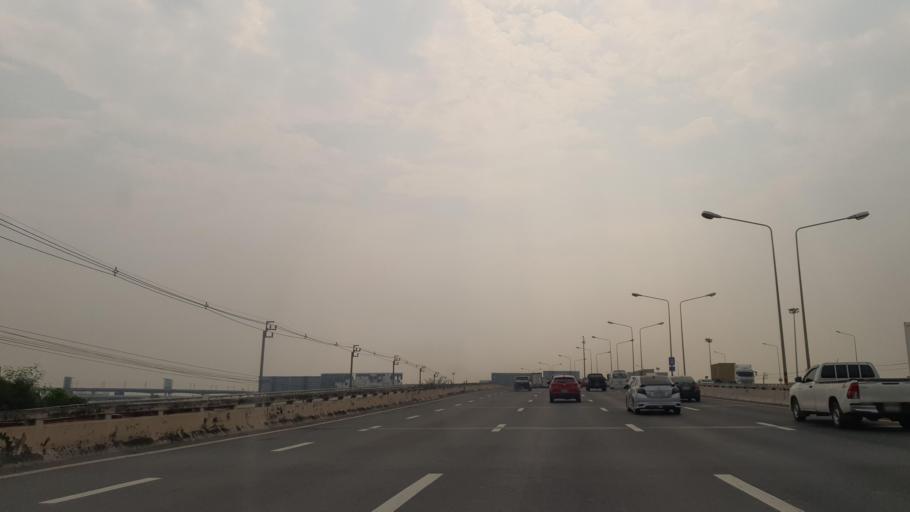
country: TH
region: Bangkok
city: Lat Krabang
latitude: 13.7311
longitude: 100.7666
